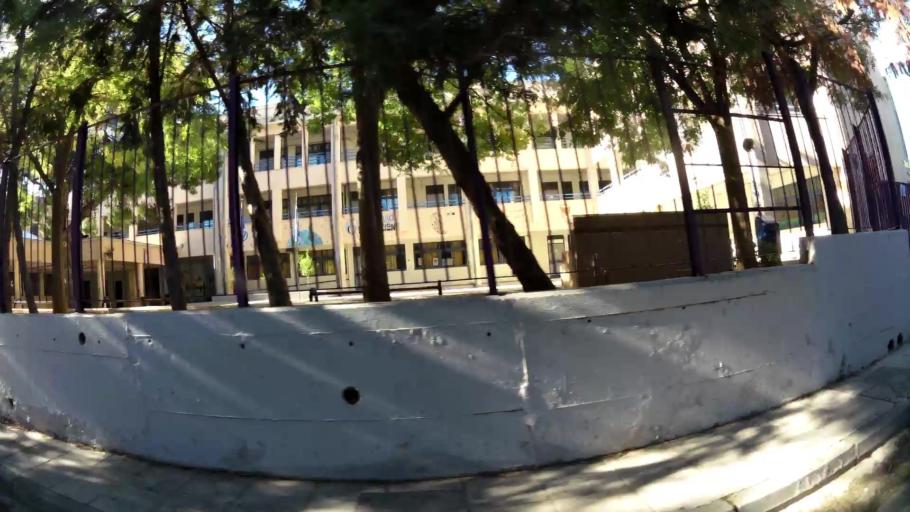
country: GR
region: Attica
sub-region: Nomarchia Athinas
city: Melissia
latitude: 38.0420
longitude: 23.8365
